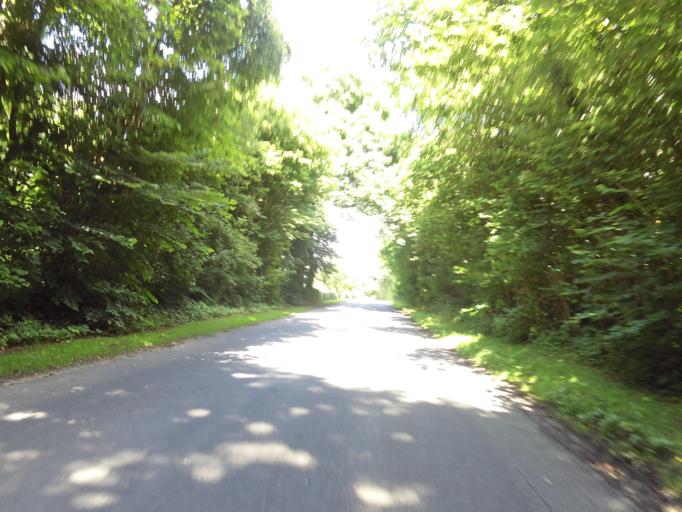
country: DK
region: South Denmark
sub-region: Vejen Kommune
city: Rodding
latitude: 55.3100
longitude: 9.1526
